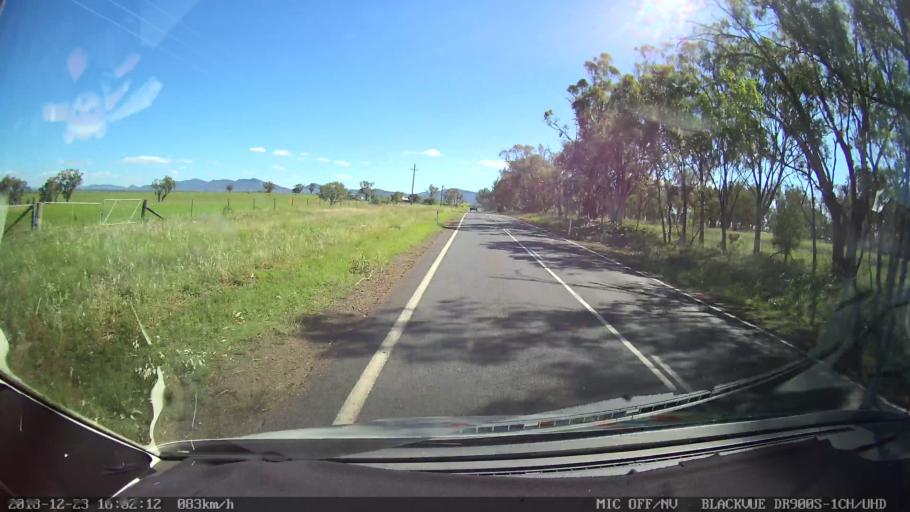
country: AU
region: New South Wales
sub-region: Tamworth Municipality
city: Phillip
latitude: -31.2297
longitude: 150.8109
